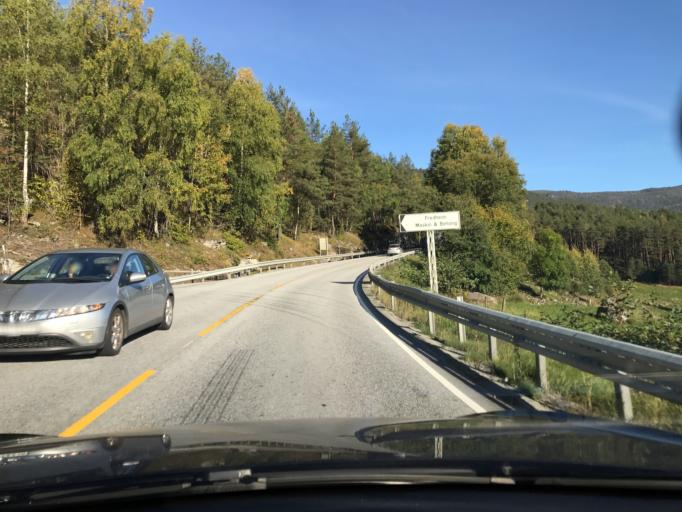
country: NO
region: Sogn og Fjordane
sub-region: Sogndal
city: Sogndalsfjora
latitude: 61.2077
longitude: 7.1744
